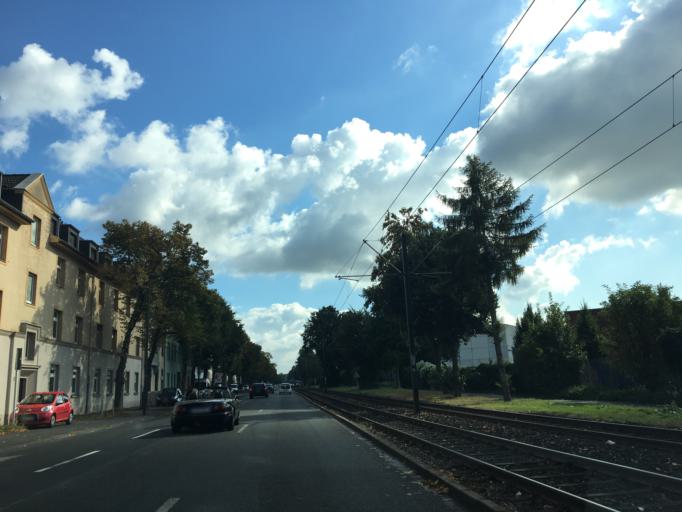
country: DE
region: North Rhine-Westphalia
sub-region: Regierungsbezirk Dusseldorf
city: Dormagen
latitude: 51.1689
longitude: 6.8422
